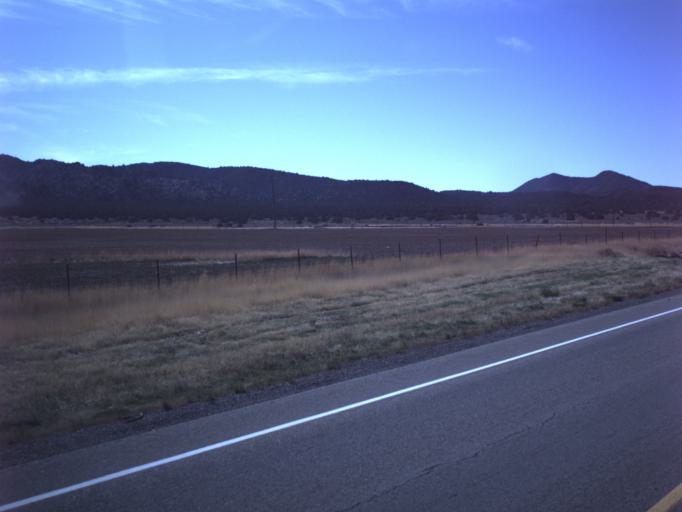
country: US
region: Utah
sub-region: Juab County
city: Nephi
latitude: 39.4650
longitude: -111.9000
